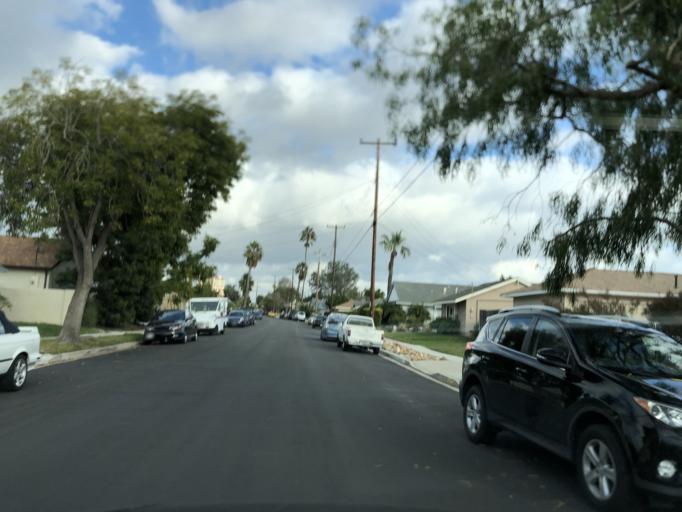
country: US
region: California
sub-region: San Diego County
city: La Jolla
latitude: 32.8168
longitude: -117.1909
